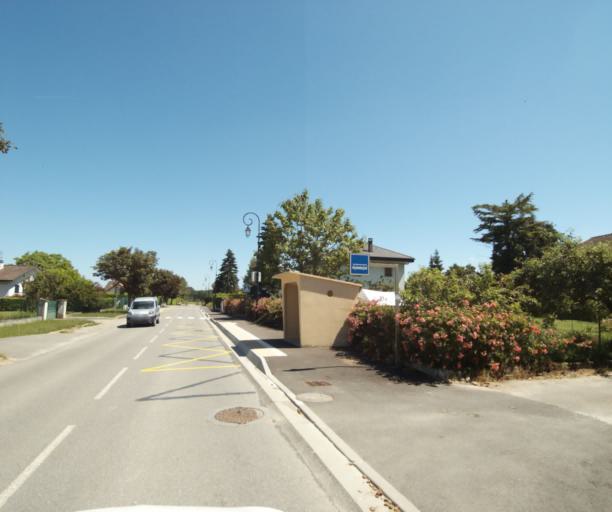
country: FR
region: Rhone-Alpes
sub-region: Departement de la Haute-Savoie
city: Veigy-Foncenex
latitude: 46.2758
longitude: 6.2582
